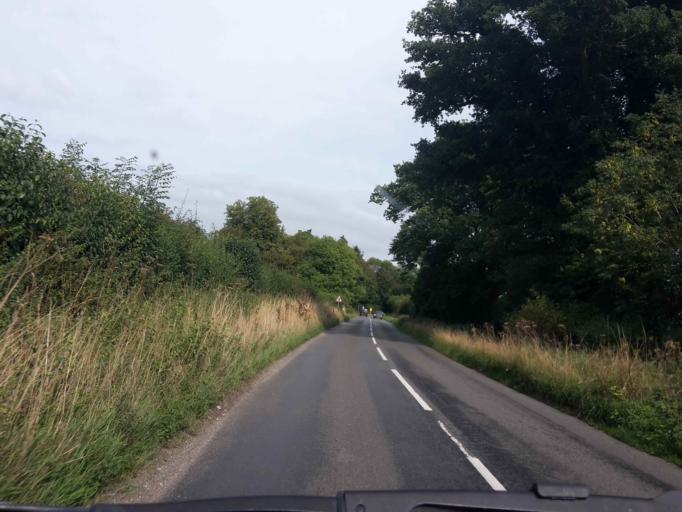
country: GB
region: England
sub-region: Oxfordshire
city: Rotherfield Peppard
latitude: 51.5457
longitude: -0.9490
